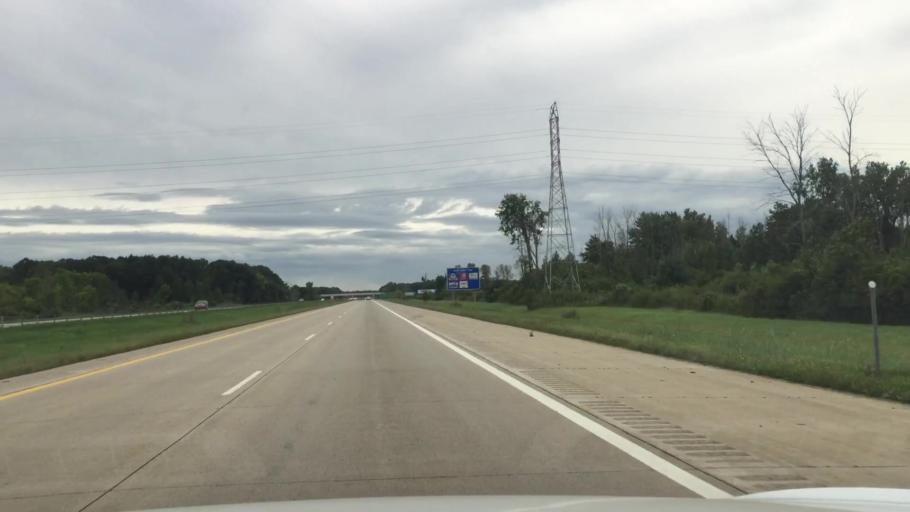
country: US
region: Michigan
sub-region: Saint Clair County
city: Marysville
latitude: 42.9291
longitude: -82.5068
